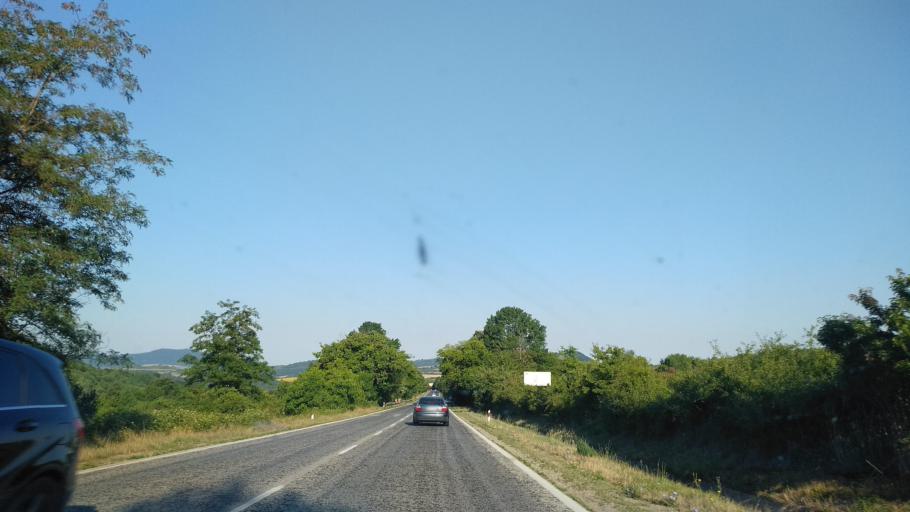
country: BG
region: Gabrovo
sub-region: Obshtina Sevlievo
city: Sevlievo
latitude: 43.0495
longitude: 24.9169
